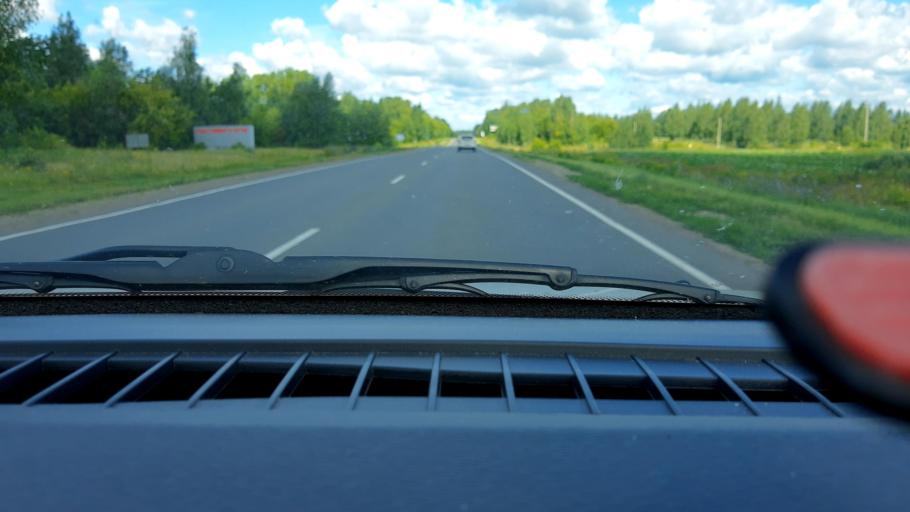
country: RU
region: Nizjnij Novgorod
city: Arzamas
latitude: 55.2835
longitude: 43.9520
